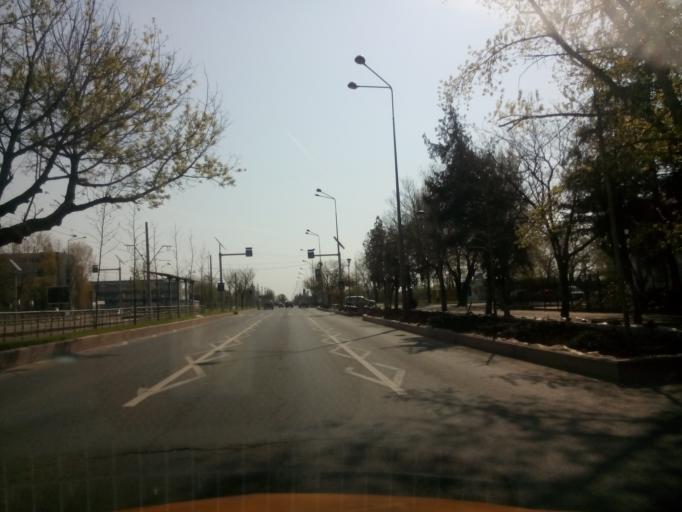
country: RO
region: Ilfov
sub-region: Comuna Glina
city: Catelu
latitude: 44.4078
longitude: 26.1917
